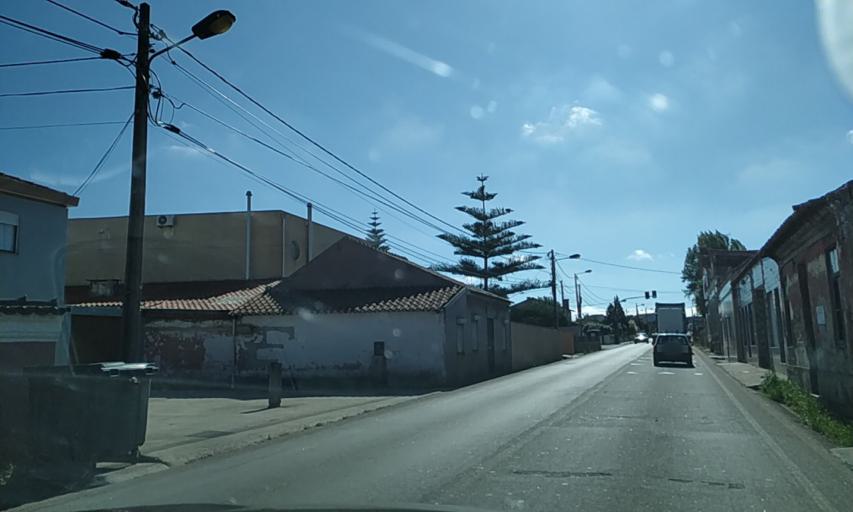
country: PT
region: Aveiro
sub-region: Aveiro
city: Eixo
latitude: 40.6792
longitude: -8.5945
